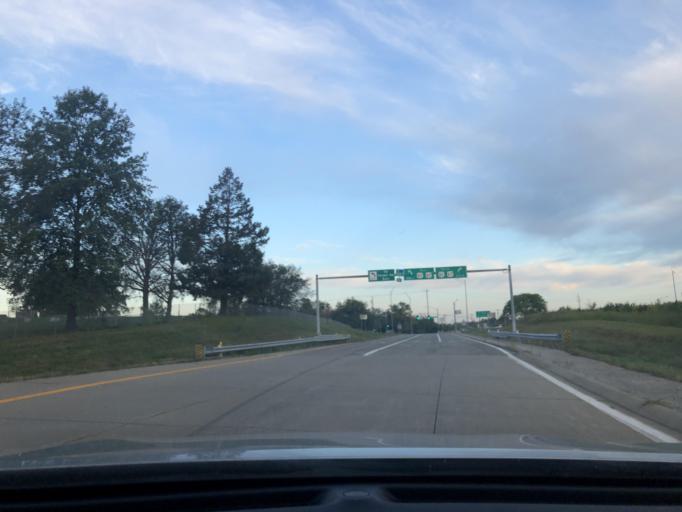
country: US
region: Missouri
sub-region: Saint Louis County
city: Mehlville
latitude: 38.5012
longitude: -90.3292
